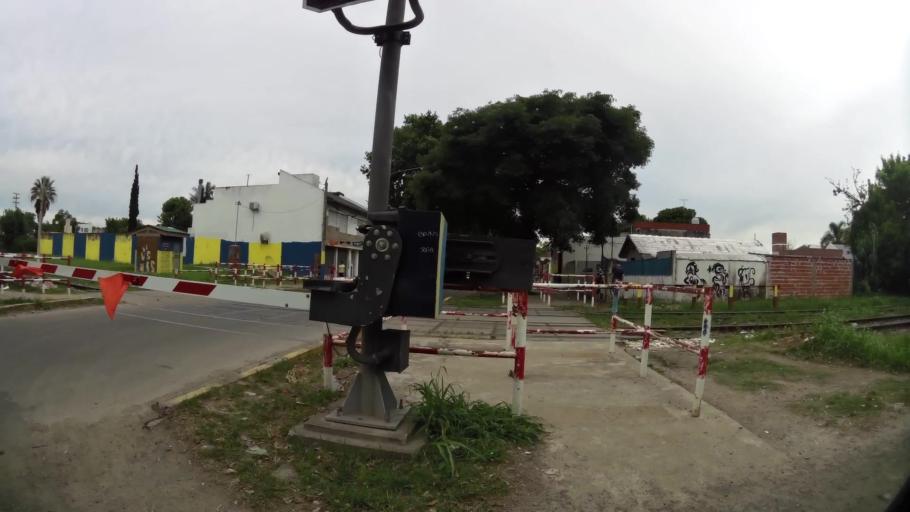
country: AR
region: Santa Fe
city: Granadero Baigorria
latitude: -32.8956
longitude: -60.6983
